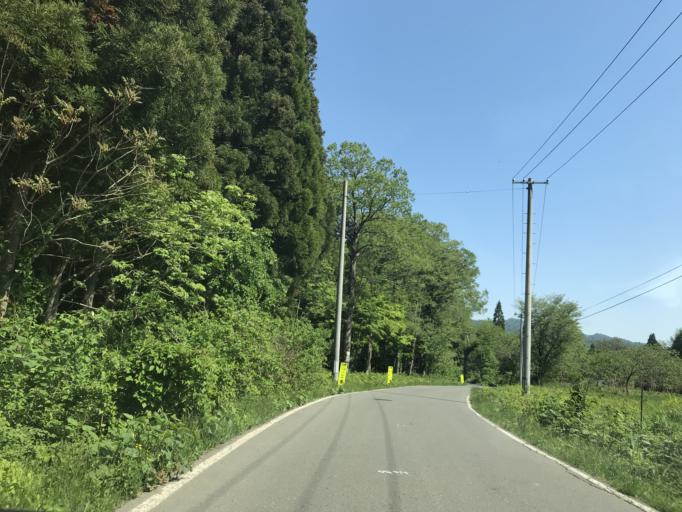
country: JP
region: Iwate
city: Shizukuishi
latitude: 39.5621
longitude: 140.8393
